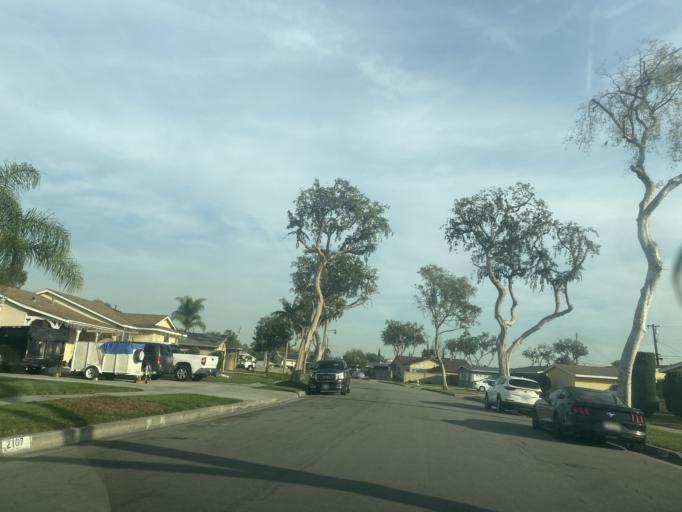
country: US
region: California
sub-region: Orange County
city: Buena Park
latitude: 33.8555
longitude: -117.9656
